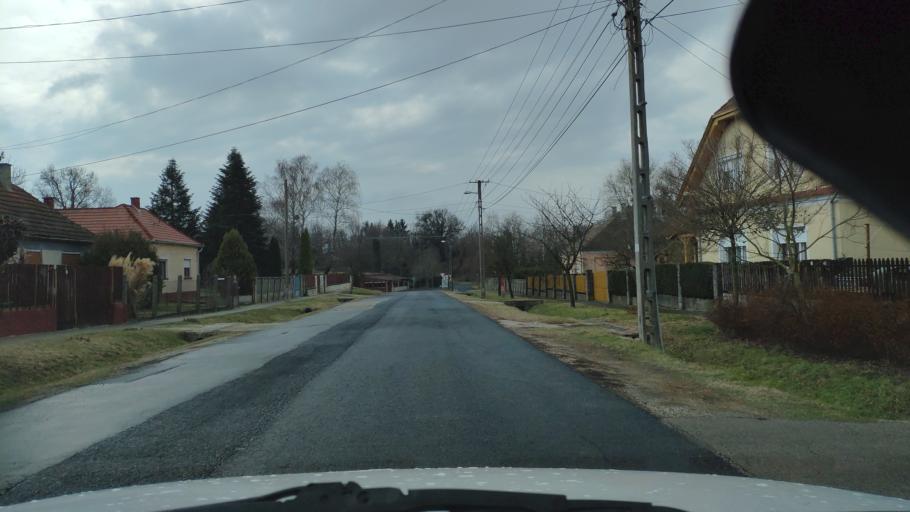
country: HU
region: Zala
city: Nagykanizsa
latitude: 46.4122
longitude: 16.9985
